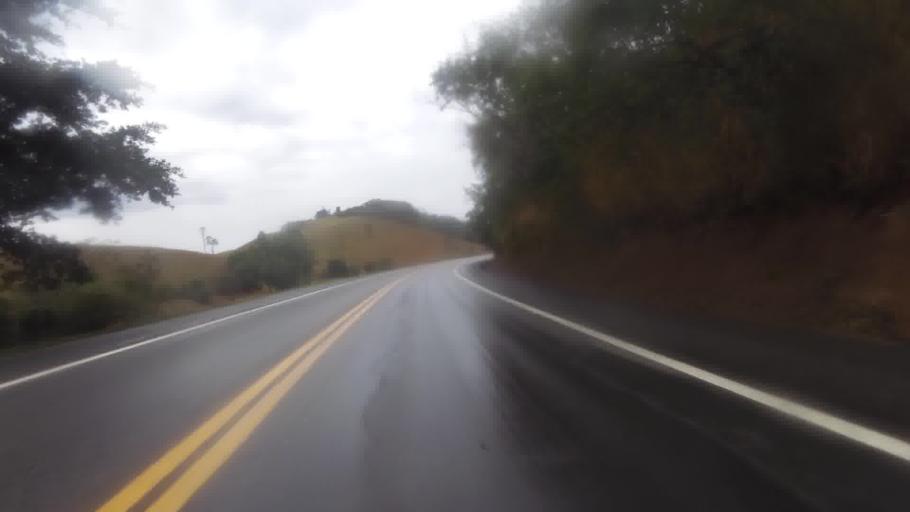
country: BR
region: Espirito Santo
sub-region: Cachoeiro De Itapemirim
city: Cachoeiro de Itapemirim
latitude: -21.0162
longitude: -41.1487
